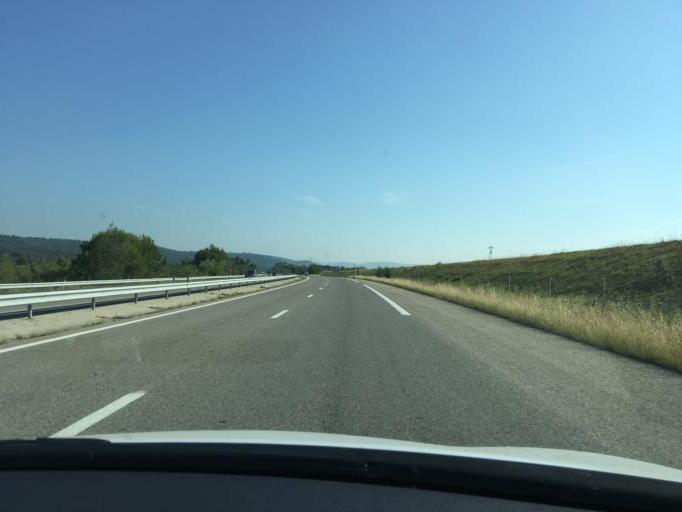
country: FR
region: Provence-Alpes-Cote d'Azur
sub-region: Departement du Vaucluse
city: Beaumont-de-Pertuis
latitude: 43.7112
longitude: 5.7356
